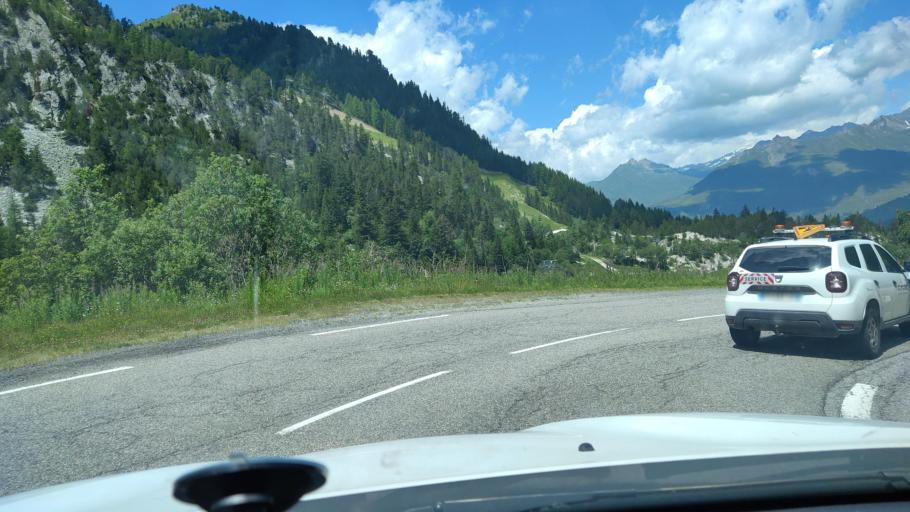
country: FR
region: Rhone-Alpes
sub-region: Departement de la Savoie
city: Seez
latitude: 45.5795
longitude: 6.8336
